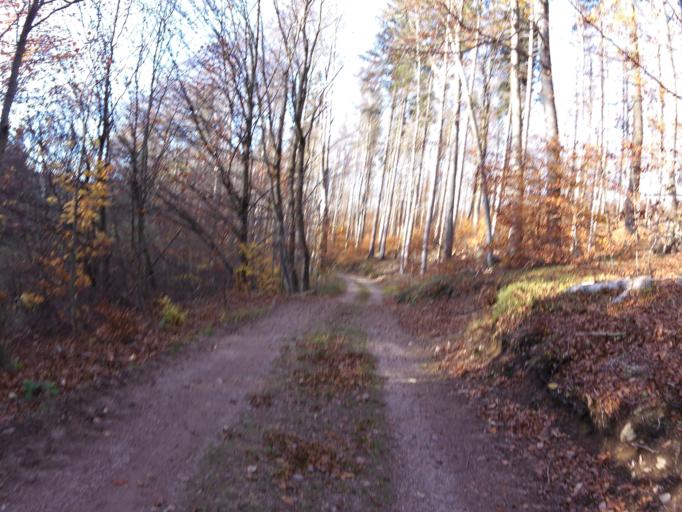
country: DE
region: Thuringia
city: Ruhla
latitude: 50.8728
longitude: 10.4003
